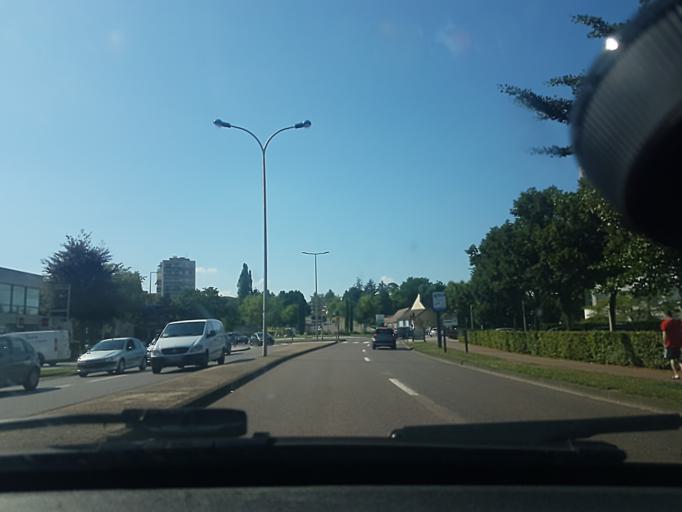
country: FR
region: Bourgogne
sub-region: Departement de Saone-et-Loire
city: Chalon-sur-Saone
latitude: 46.7898
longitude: 4.8632
